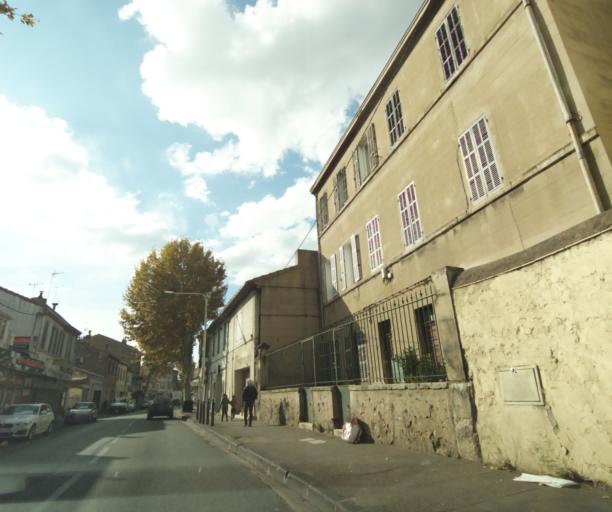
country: FR
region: Provence-Alpes-Cote d'Azur
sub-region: Departement des Bouches-du-Rhone
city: Marseille 13
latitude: 43.3277
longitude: 5.4244
